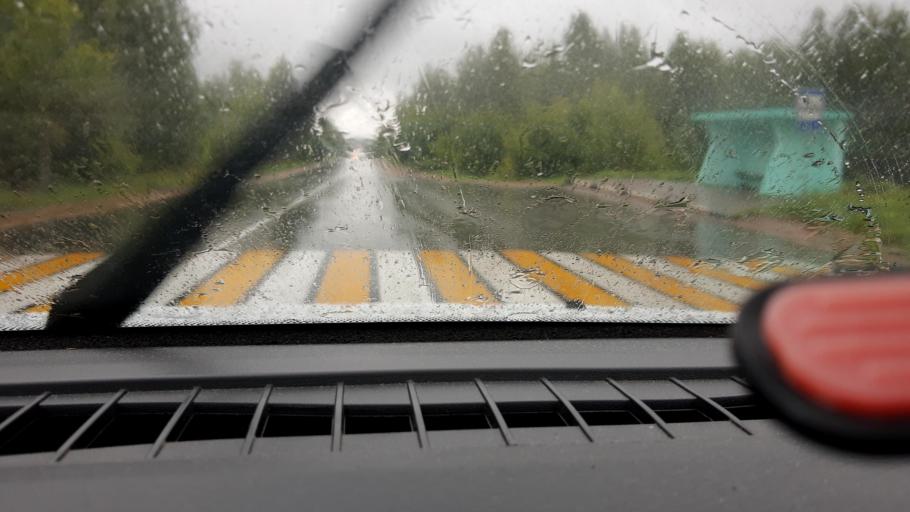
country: RU
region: Nizjnij Novgorod
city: Lyskovo
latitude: 56.0163
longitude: 45.0147
